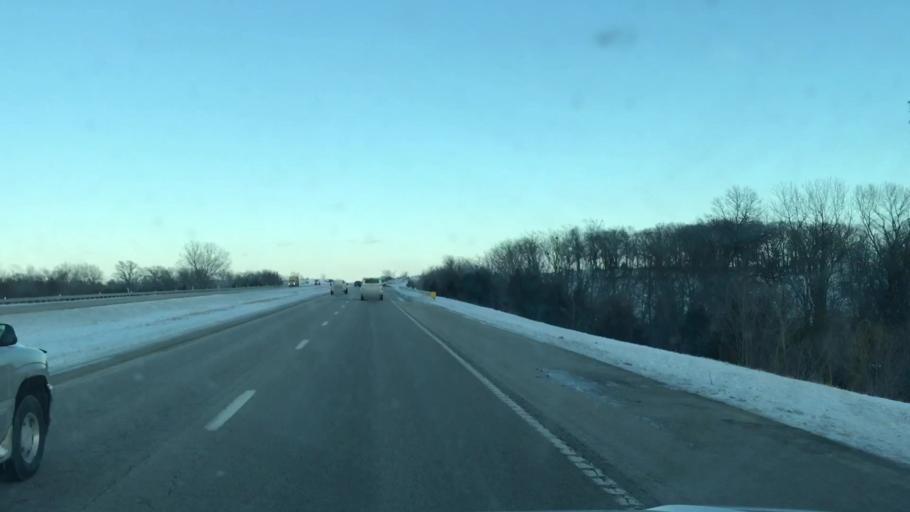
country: US
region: Missouri
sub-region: Buchanan County
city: Saint Joseph
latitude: 39.7476
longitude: -94.7025
